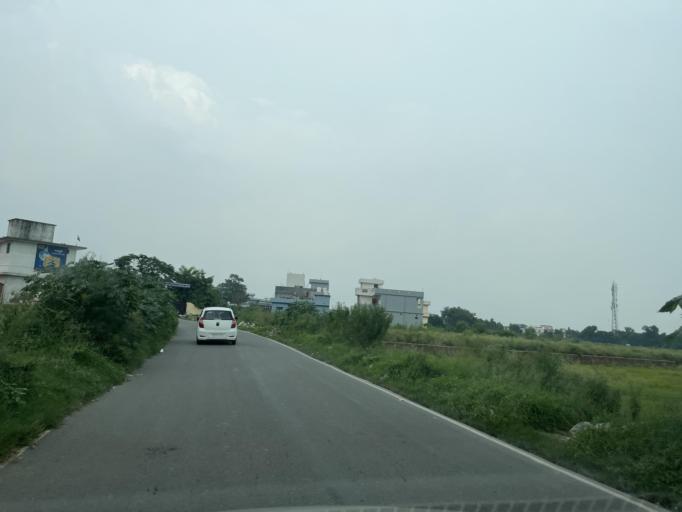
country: IN
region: Uttarakhand
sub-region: Naini Tal
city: Haldwani
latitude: 29.1885
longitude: 79.4785
